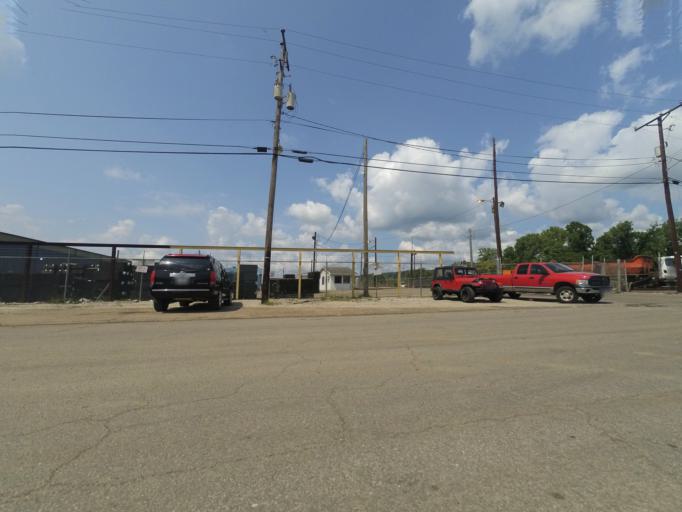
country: US
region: West Virginia
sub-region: Cabell County
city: Huntington
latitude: 38.4283
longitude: -82.4239
